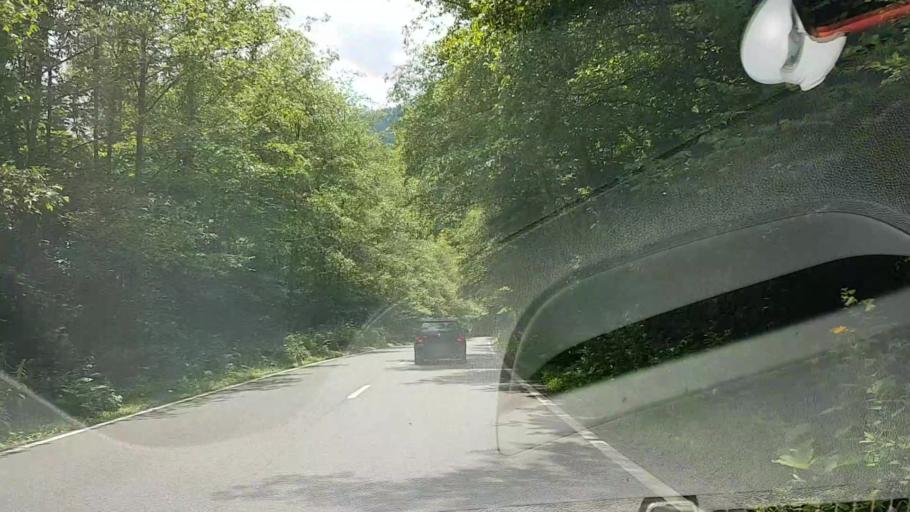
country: RO
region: Suceava
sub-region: Comuna Crucea
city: Crucea
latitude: 47.2961
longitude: 25.6323
